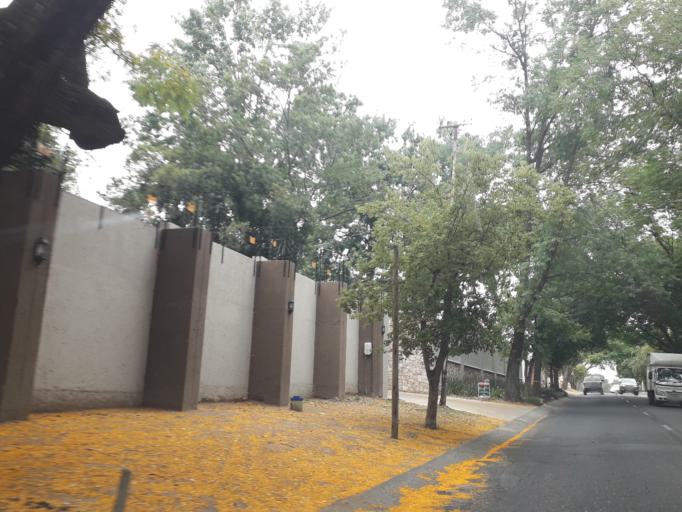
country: ZA
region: Gauteng
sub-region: City of Johannesburg Metropolitan Municipality
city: Midrand
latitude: -26.0437
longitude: 28.0439
